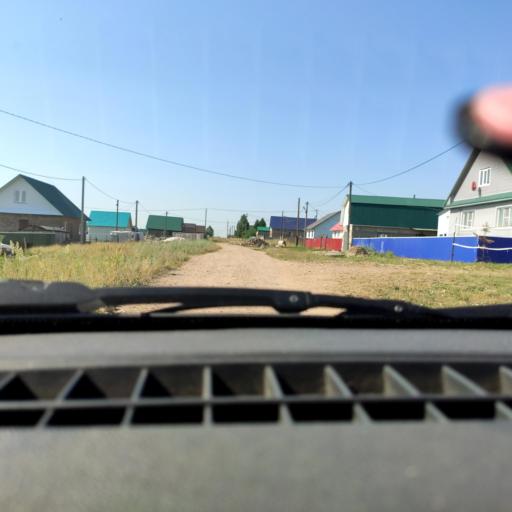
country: RU
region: Bashkortostan
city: Blagoveshchensk
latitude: 54.9407
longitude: 56.1344
